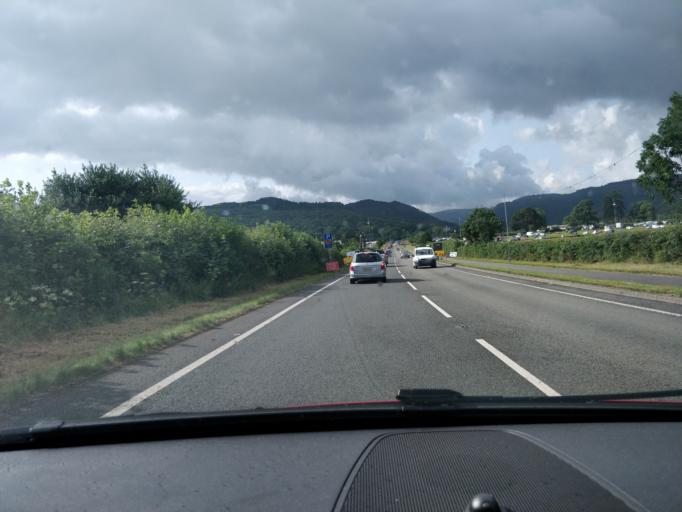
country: GB
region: Wales
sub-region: Conwy
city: Llanrwst
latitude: 53.1170
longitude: -3.7809
